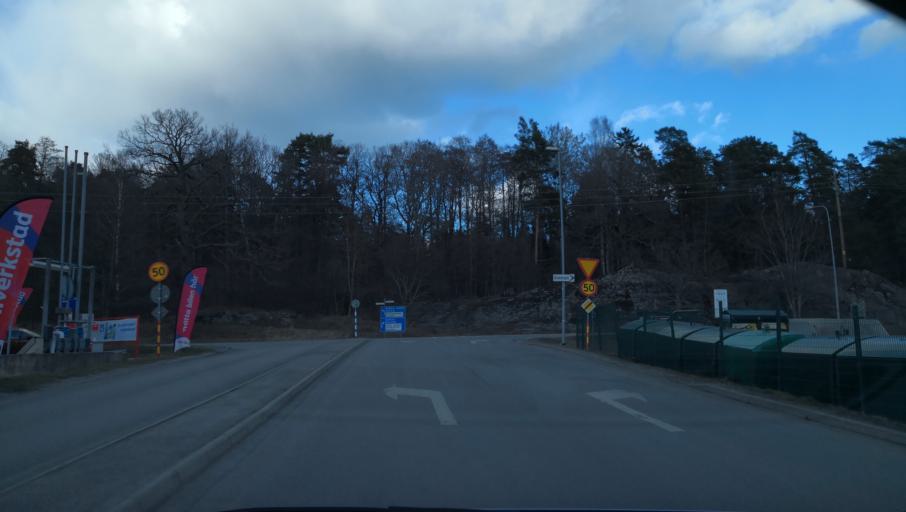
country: SE
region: Stockholm
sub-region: Varmdo Kommun
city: Gustavsberg
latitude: 59.3285
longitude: 18.3929
